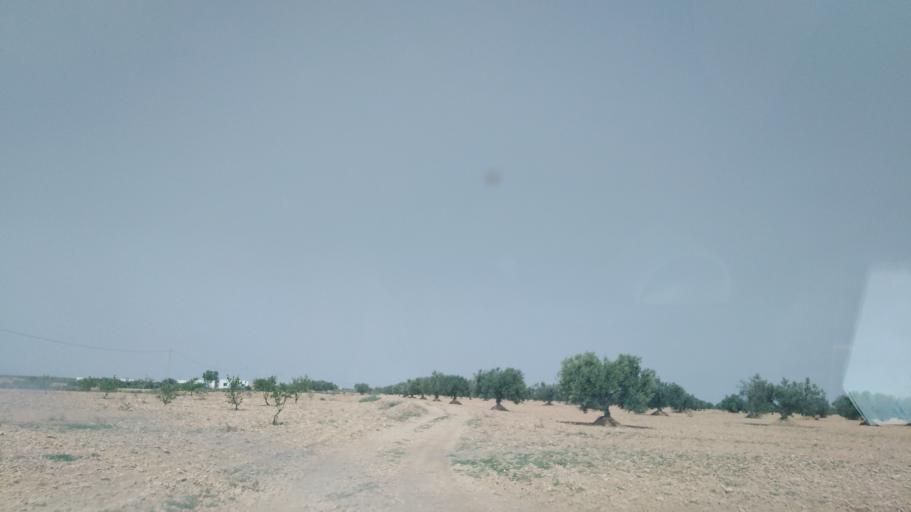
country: TN
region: Safaqis
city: Sfax
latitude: 34.6532
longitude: 10.5570
